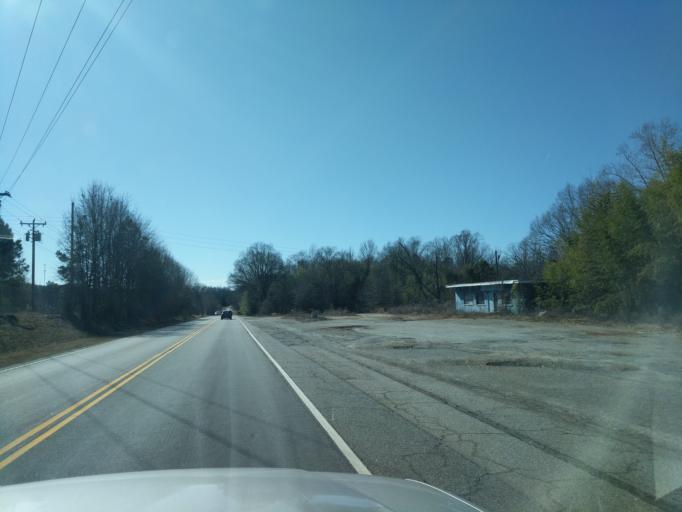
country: US
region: South Carolina
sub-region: Anderson County
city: Homeland Park
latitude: 34.4589
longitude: -82.6909
